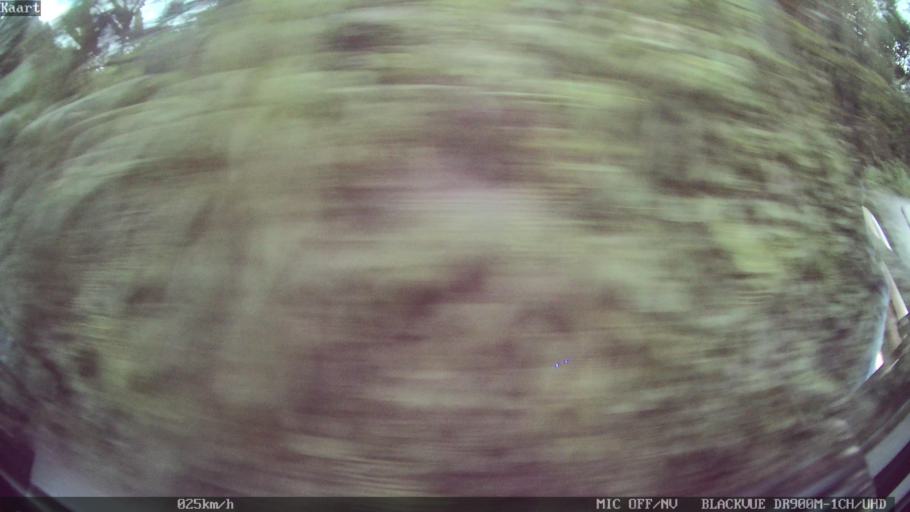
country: ID
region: Bali
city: Peneng
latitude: -8.3627
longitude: 115.1801
